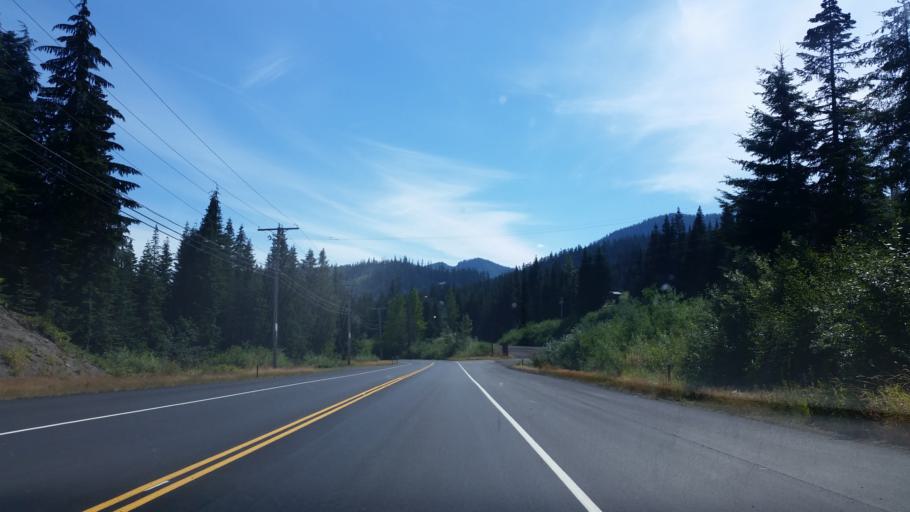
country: US
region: Washington
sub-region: King County
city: Tanner
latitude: 47.4072
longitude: -121.4117
